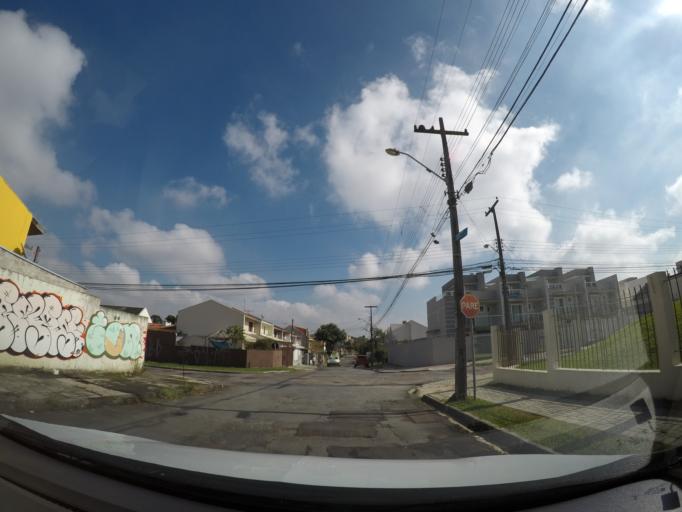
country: BR
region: Parana
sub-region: Sao Jose Dos Pinhais
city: Sao Jose dos Pinhais
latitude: -25.4920
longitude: -49.2196
